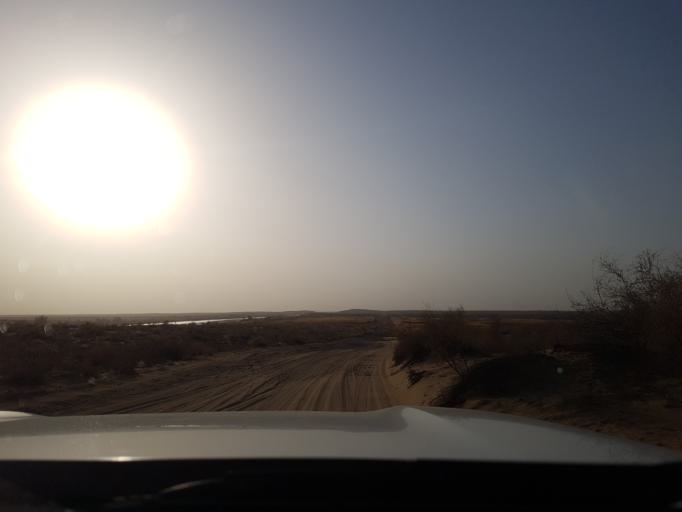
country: UZ
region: Xorazm
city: Hazorasp
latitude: 41.1698
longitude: 60.7999
